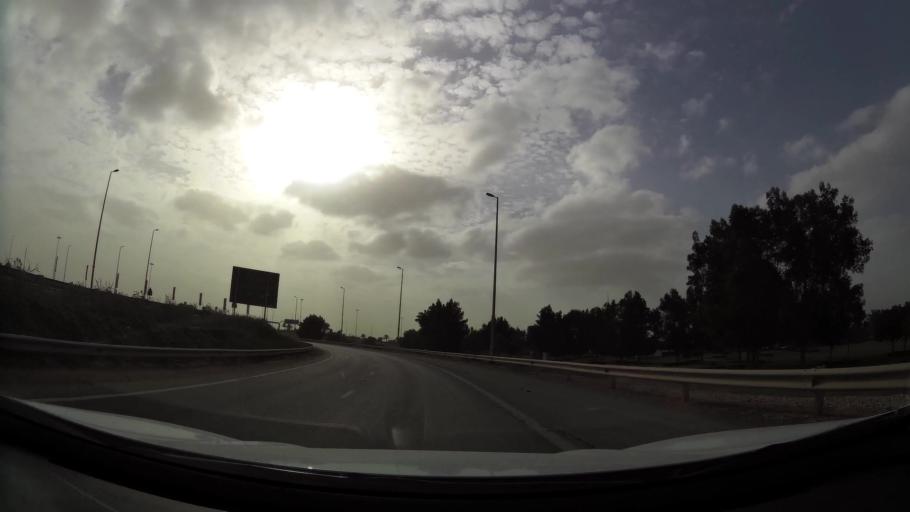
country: AE
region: Abu Dhabi
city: Abu Dhabi
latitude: 24.4912
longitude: 54.6296
